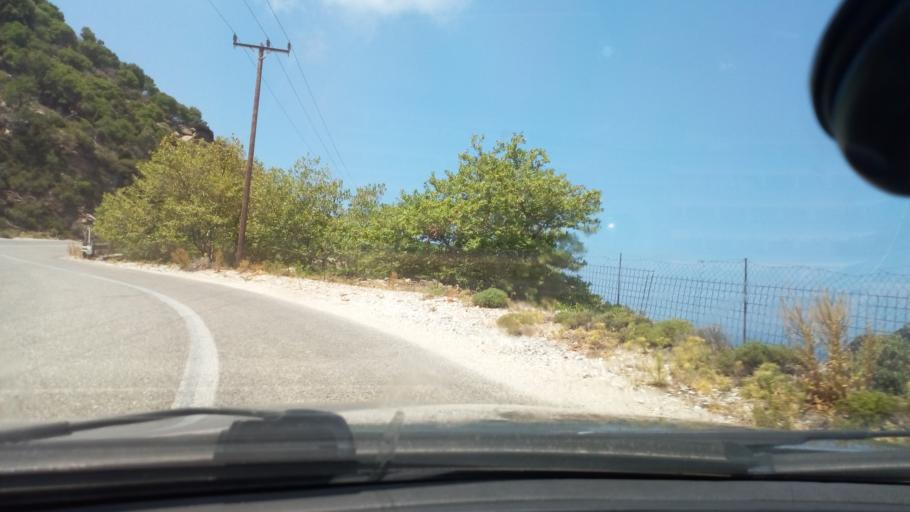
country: GR
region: North Aegean
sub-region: Nomos Samou
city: Agios Kirykos
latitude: 37.6370
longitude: 26.2572
